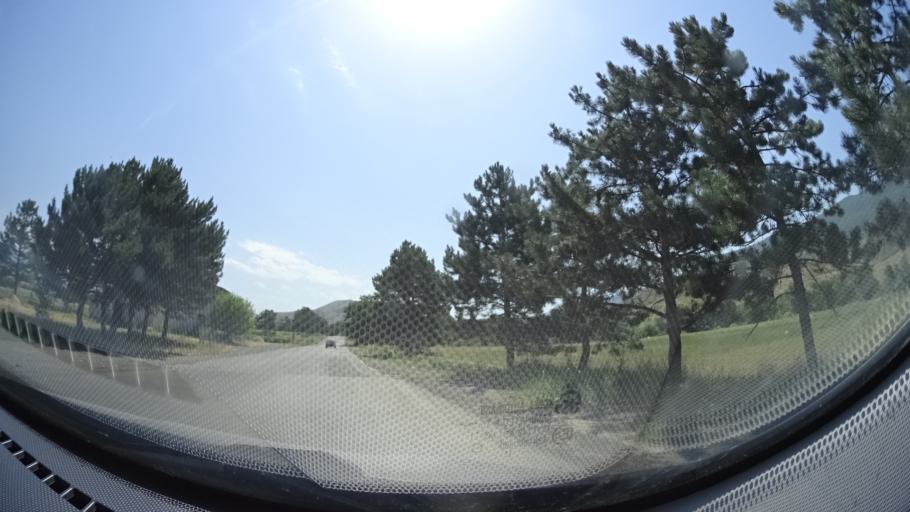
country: GE
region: Samtskhe-Javakheti
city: Aspindza
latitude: 41.6150
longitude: 43.1219
